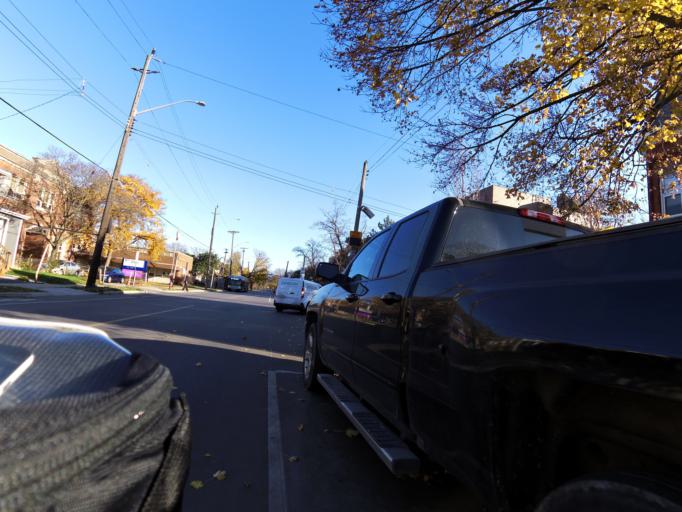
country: CA
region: Ontario
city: Hamilton
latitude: 43.2455
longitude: -79.8381
